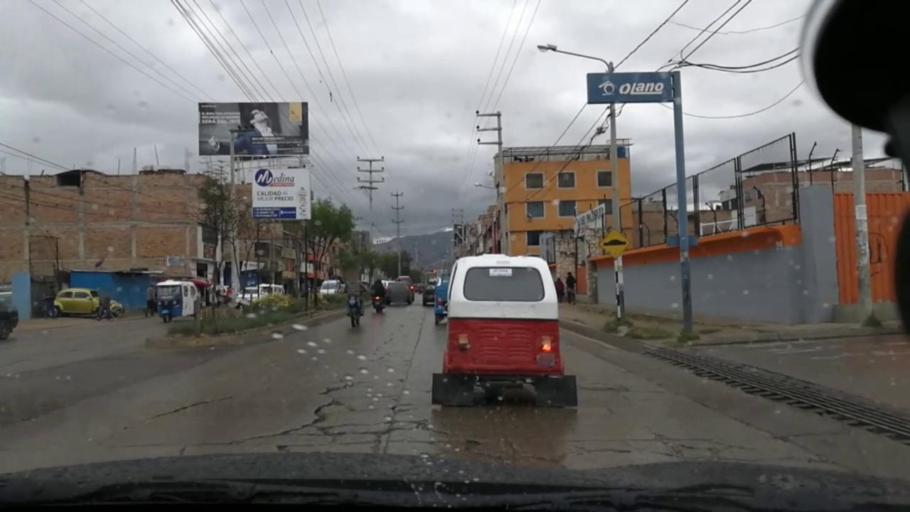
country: PE
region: Cajamarca
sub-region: Provincia de Cajamarca
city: Cajamarca
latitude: -7.1622
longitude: -78.5035
